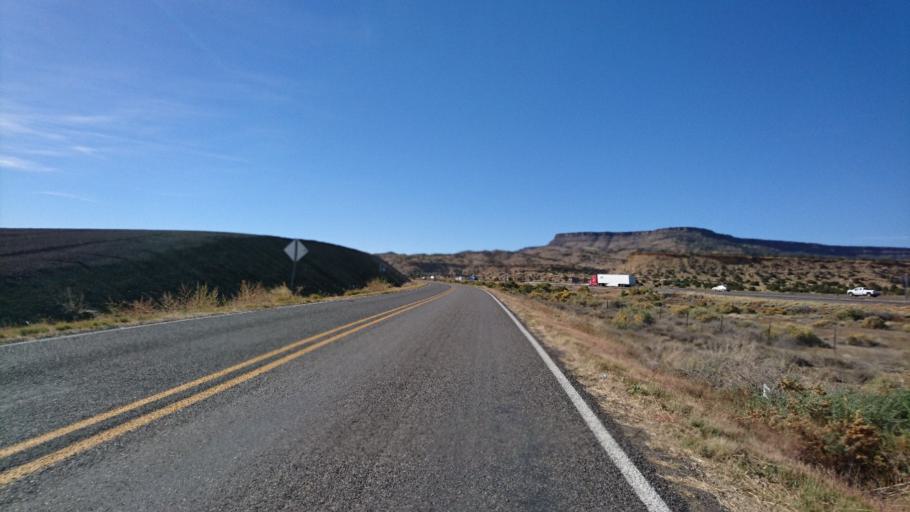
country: US
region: New Mexico
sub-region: Cibola County
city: Skyline-Ganipa
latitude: 35.0729
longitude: -107.6591
